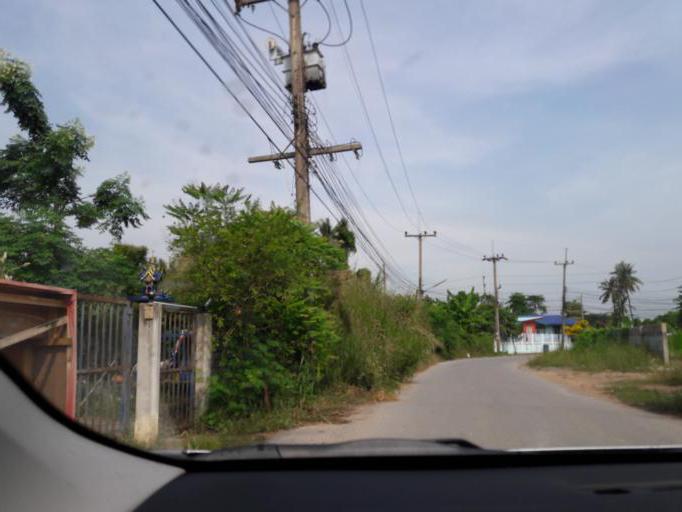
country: TH
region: Ang Thong
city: Ang Thong
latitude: 14.5848
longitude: 100.4622
